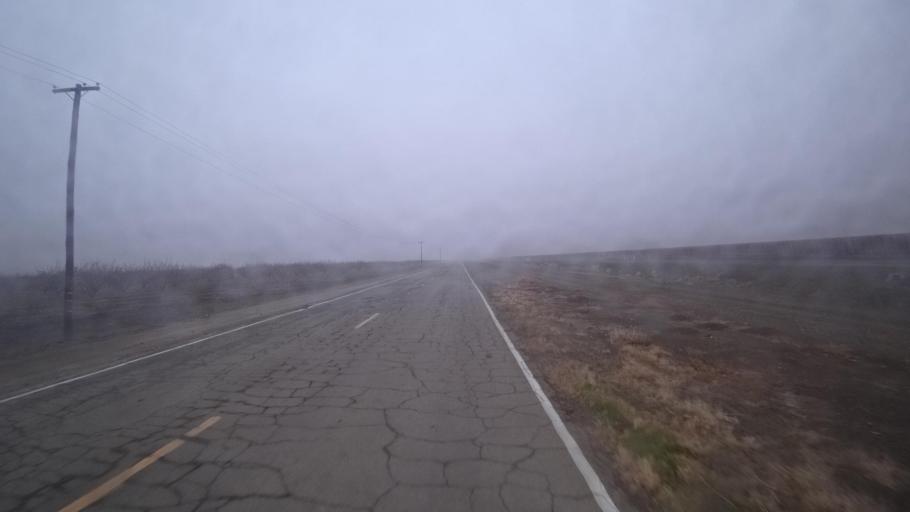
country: US
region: California
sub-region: Kern County
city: Lost Hills
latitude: 35.5182
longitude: -119.6174
